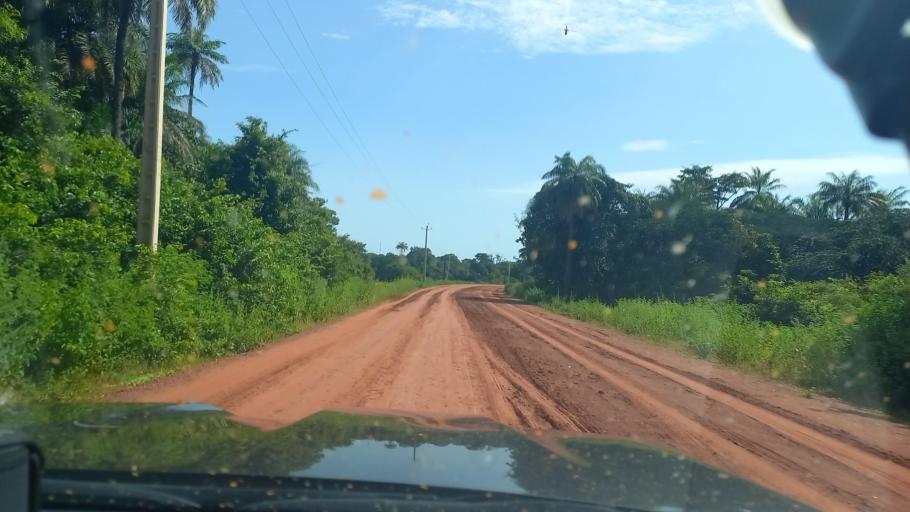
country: SN
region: Ziguinchor
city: Adeane
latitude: 12.6661
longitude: -16.1033
